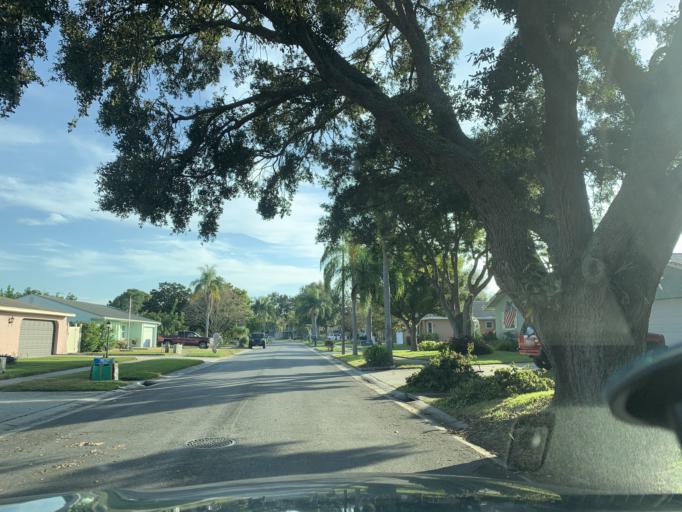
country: US
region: Florida
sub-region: Pinellas County
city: Ridgecrest
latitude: 27.8914
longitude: -82.7990
